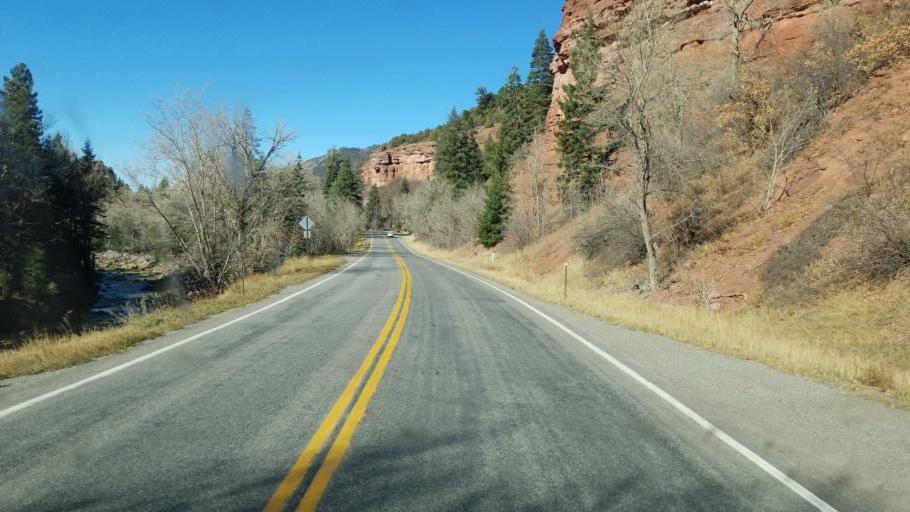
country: US
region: Colorado
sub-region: Ouray County
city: Ouray
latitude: 38.0567
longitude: -107.6903
